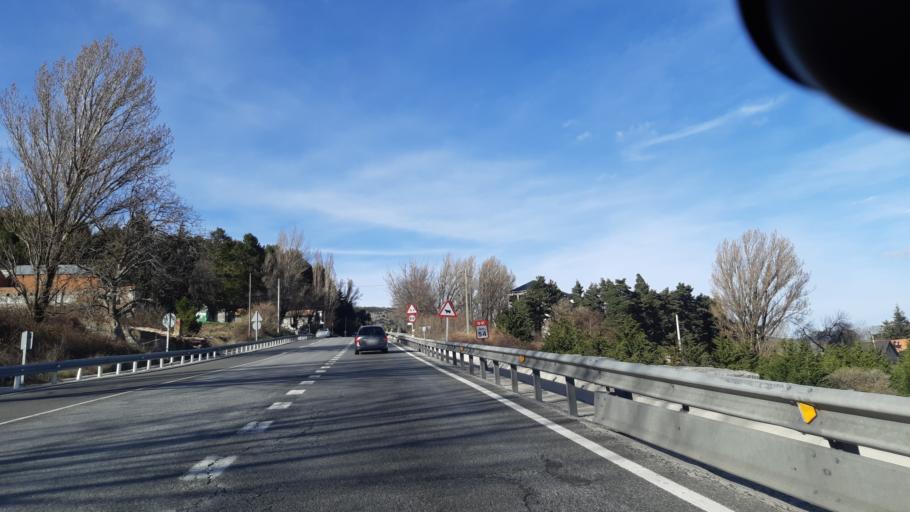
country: ES
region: Madrid
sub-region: Provincia de Madrid
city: Guadarrama
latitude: 40.7029
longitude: -4.1280
